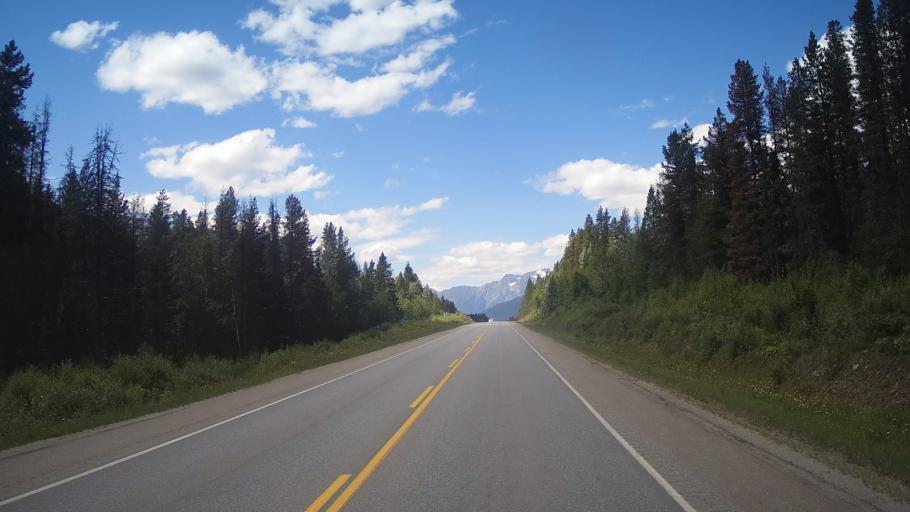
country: CA
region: Alberta
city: Jasper Park Lodge
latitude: 52.9749
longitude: -118.9592
